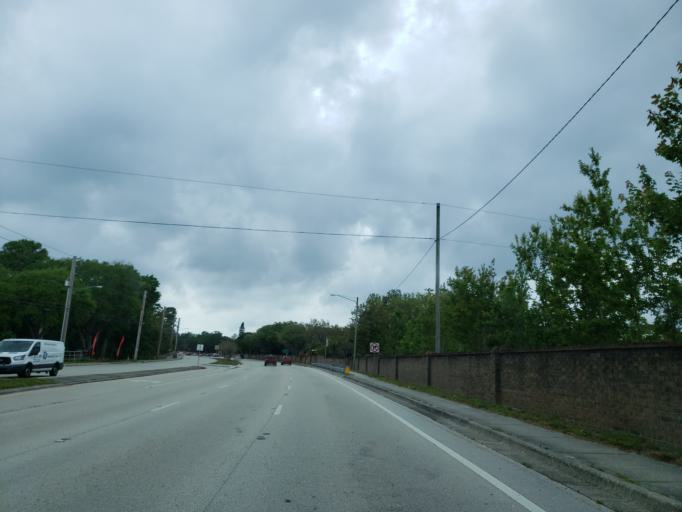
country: US
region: Florida
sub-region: Pinellas County
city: Saint George
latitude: 28.0659
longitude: -82.7168
